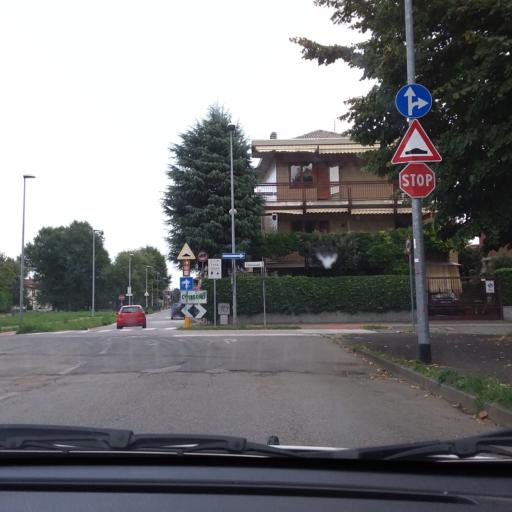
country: IT
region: Piedmont
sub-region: Provincia di Torino
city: Collegno
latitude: 45.0764
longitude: 7.5576
